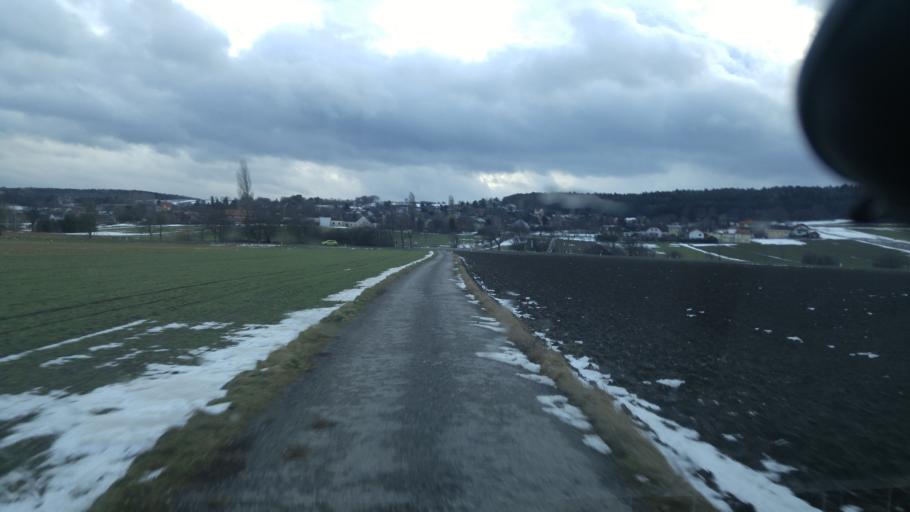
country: AT
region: Lower Austria
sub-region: Politischer Bezirk Baden
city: Hirtenberg
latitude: 47.9609
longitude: 16.1667
